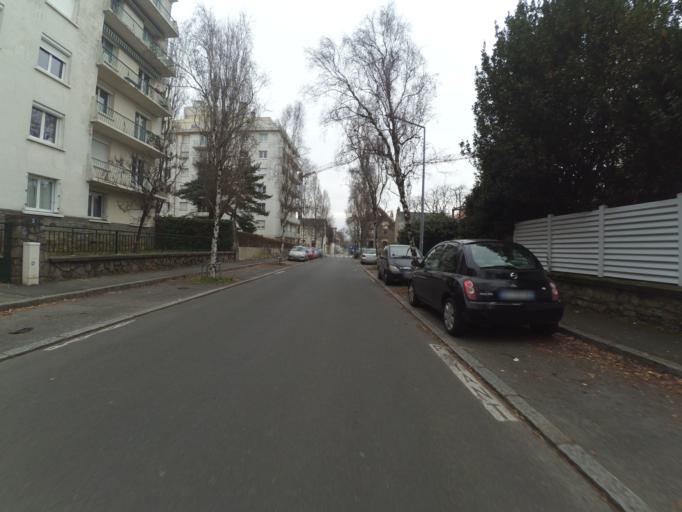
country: FR
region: Pays de la Loire
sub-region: Departement de la Loire-Atlantique
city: Nantes
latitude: 47.2256
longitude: -1.5701
